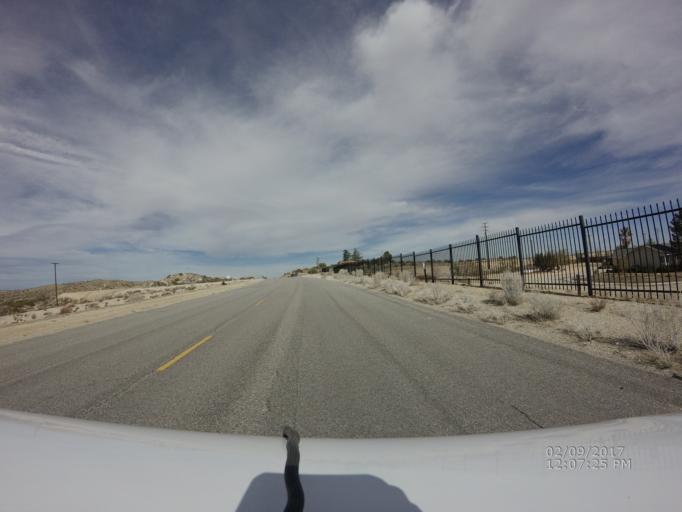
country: US
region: California
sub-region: Los Angeles County
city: Littlerock
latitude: 34.4823
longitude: -117.9132
